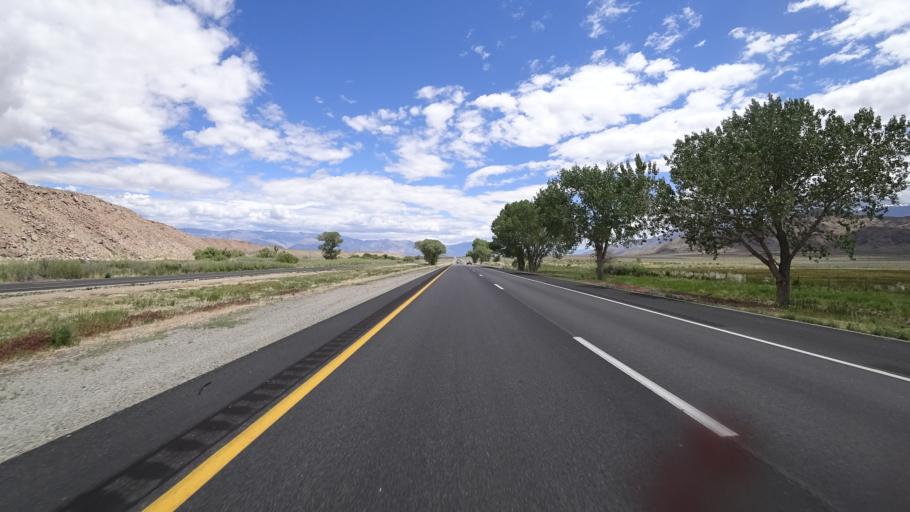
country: US
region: California
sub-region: Inyo County
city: West Bishop
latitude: 37.4040
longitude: -118.5389
